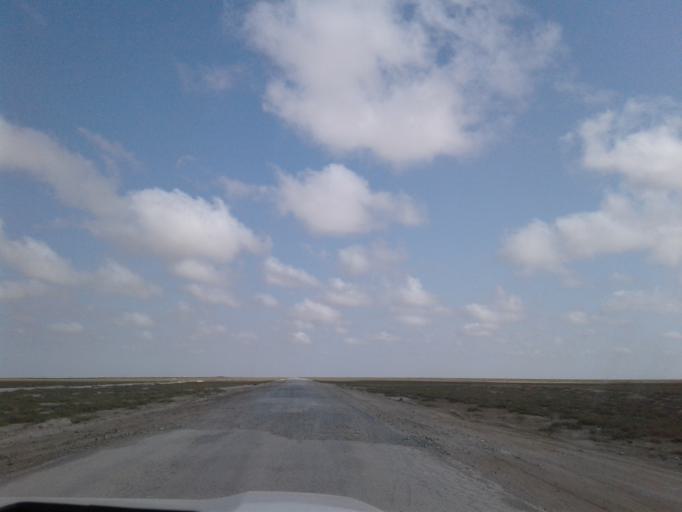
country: IR
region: Golestan
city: Gomishan
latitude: 37.6006
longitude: 53.9243
